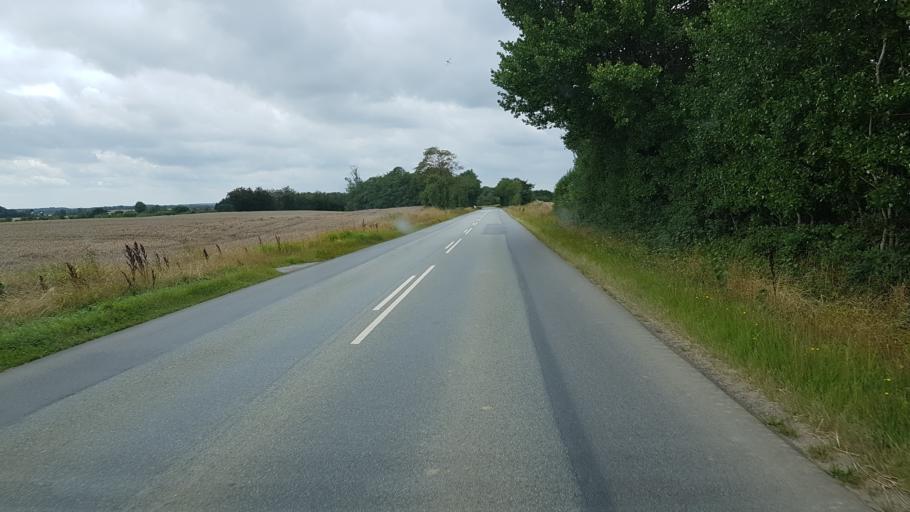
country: DK
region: South Denmark
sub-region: Kolding Kommune
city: Kolding
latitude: 55.4693
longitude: 9.3931
